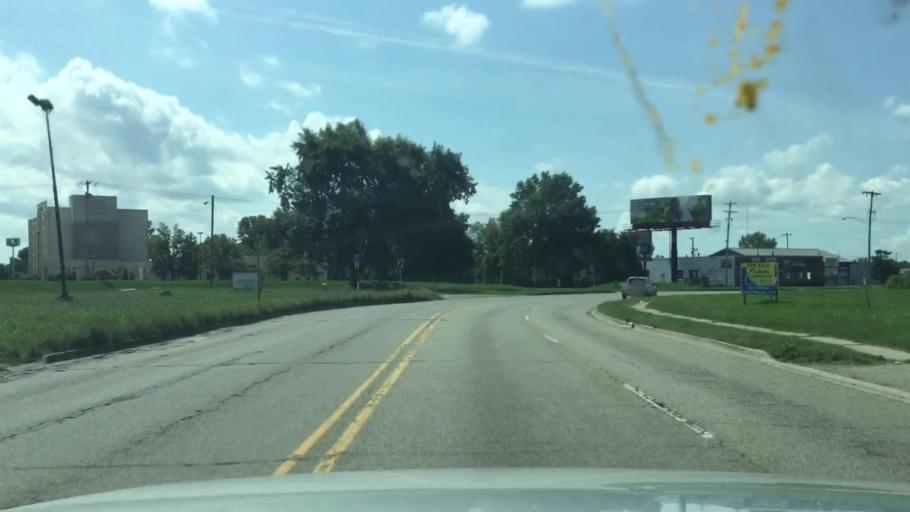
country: US
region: Michigan
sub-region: Kalamazoo County
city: Eastwood
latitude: 42.2604
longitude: -85.5344
